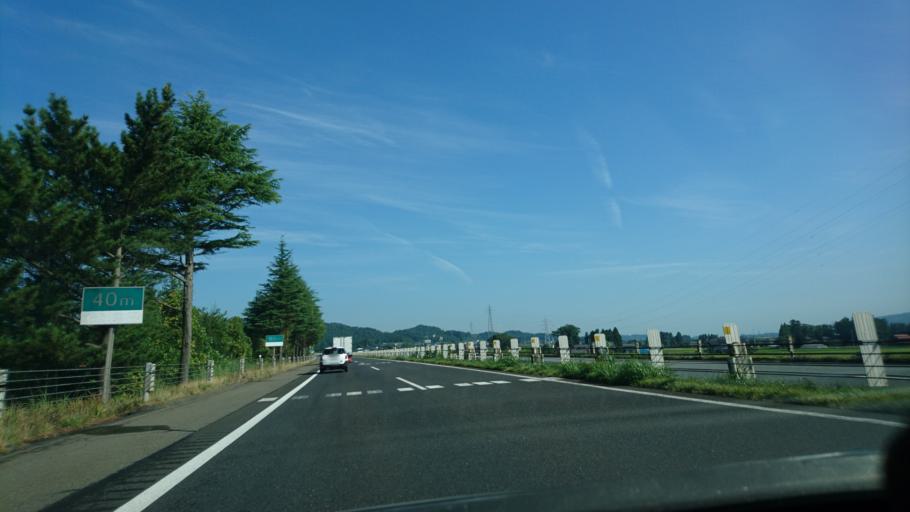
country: JP
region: Iwate
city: Ichinoseki
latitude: 38.9747
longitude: 141.1116
